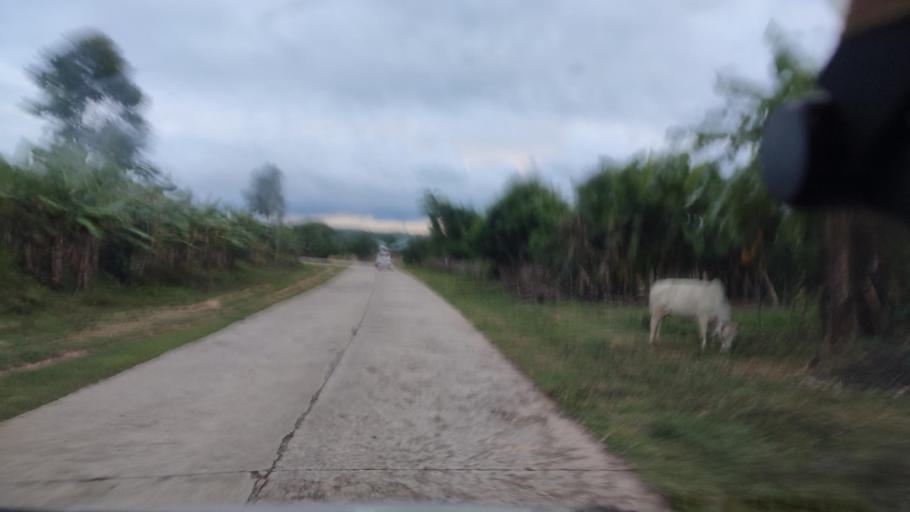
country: MM
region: Mandalay
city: Nay Pyi Taw
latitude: 19.9506
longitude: 95.9827
